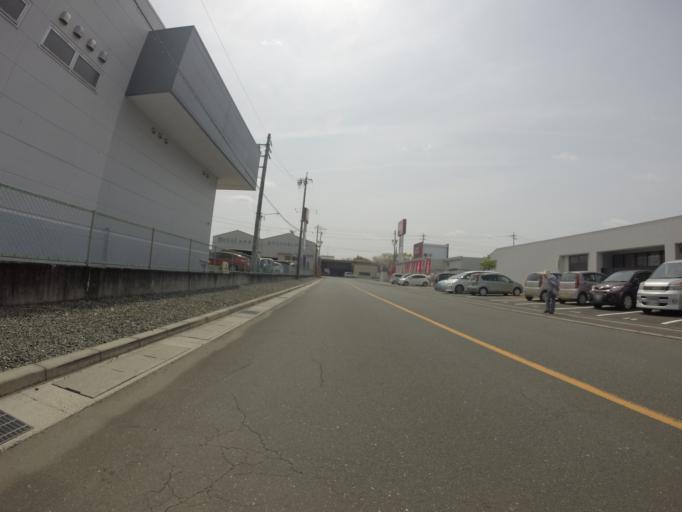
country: JP
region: Shizuoka
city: Kakegawa
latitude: 34.7751
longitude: 137.9886
